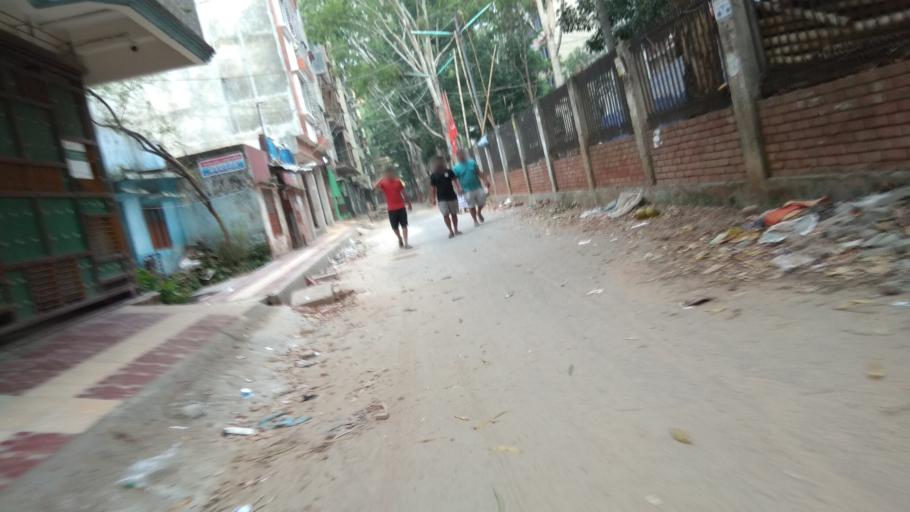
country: BD
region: Dhaka
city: Tungi
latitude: 23.8261
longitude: 90.3683
